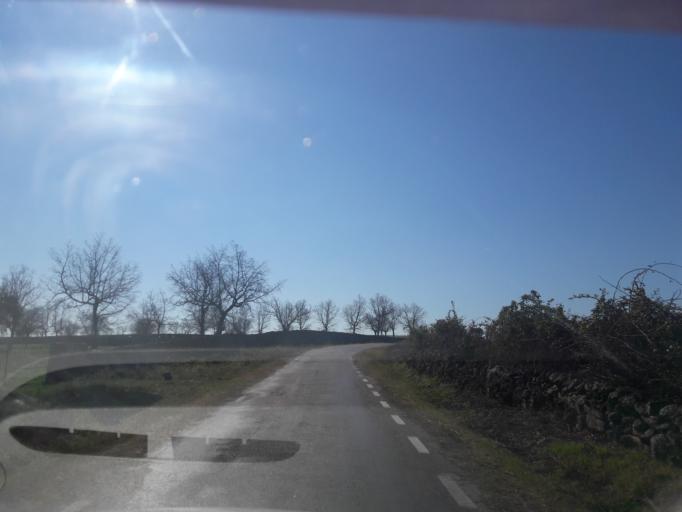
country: ES
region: Castille and Leon
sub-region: Provincia de Salamanca
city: Valsalabroso
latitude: 41.1693
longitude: -6.5027
